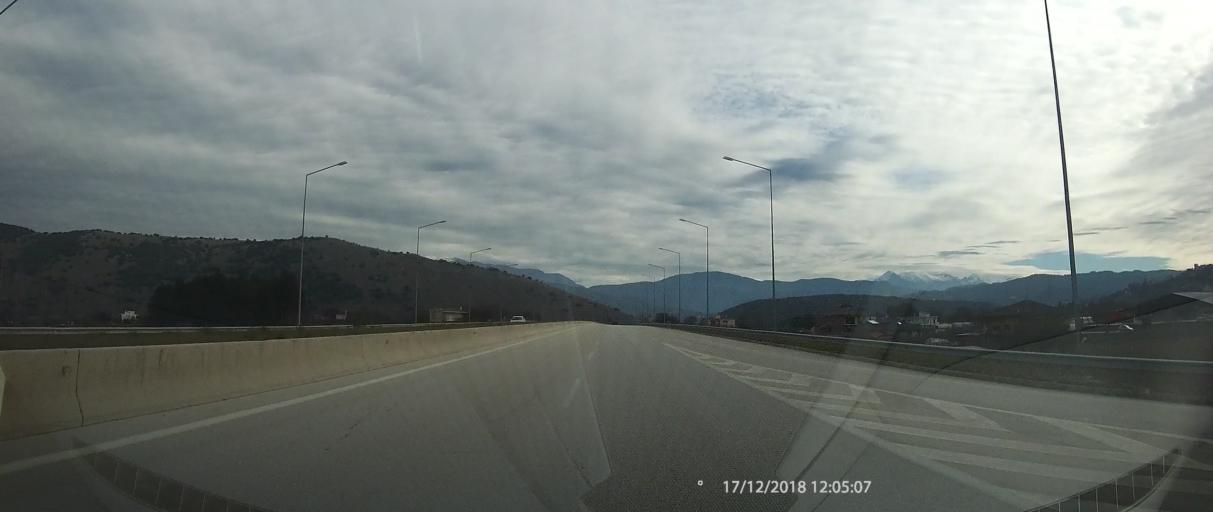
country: GR
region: Epirus
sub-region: Nomos Ioanninon
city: Koutselio
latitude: 39.6004
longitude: 20.9024
